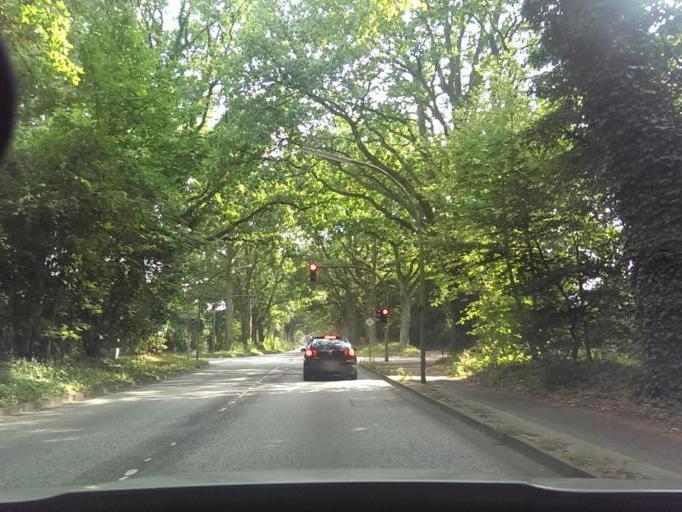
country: DE
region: Hamburg
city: Lemsahl-Mellingstedt
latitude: 53.6832
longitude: 10.0951
